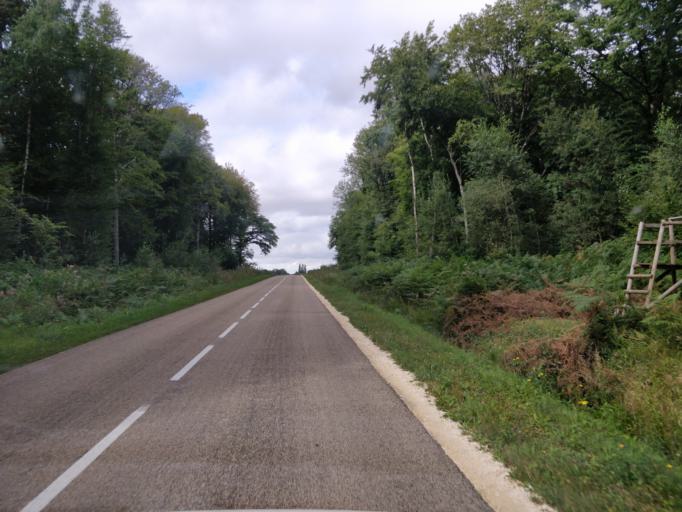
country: FR
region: Champagne-Ardenne
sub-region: Departement de l'Aube
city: Aix-en-Othe
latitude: 48.1181
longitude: 3.6682
